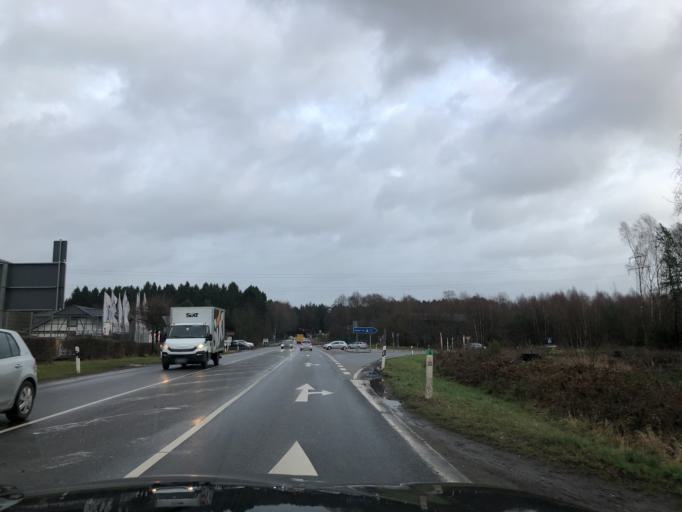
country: DE
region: Rheinland-Pfalz
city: Windhagen
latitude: 50.6498
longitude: 7.3271
